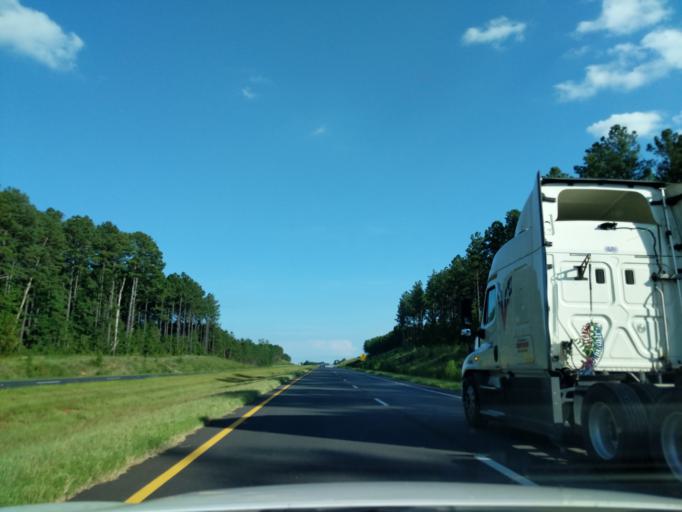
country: US
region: Georgia
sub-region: Wilkes County
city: Washington
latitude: 33.6903
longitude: -82.6470
